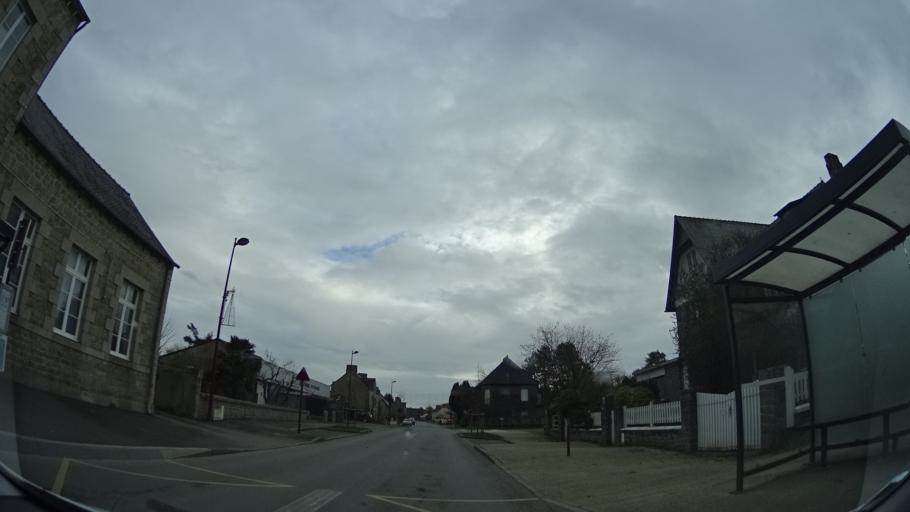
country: FR
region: Brittany
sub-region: Departement des Cotes-d'Armor
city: Evran
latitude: 48.3802
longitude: -1.9789
